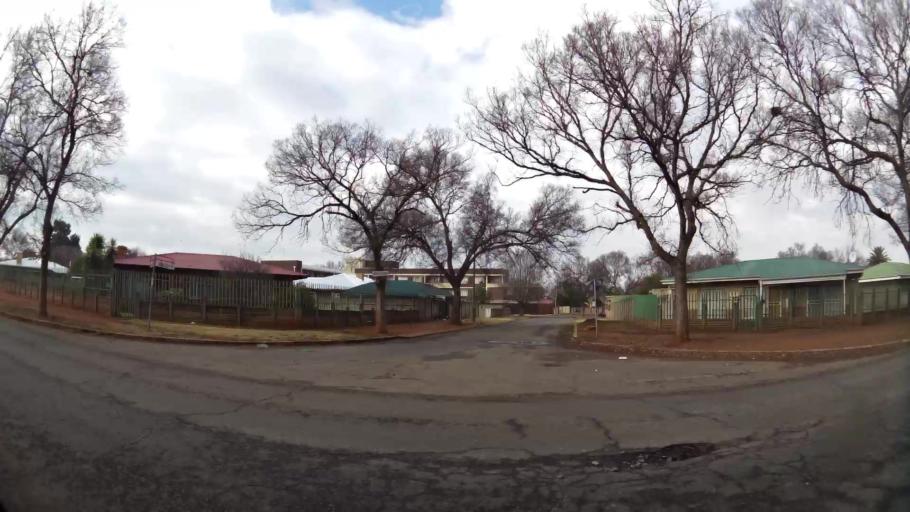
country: ZA
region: Gauteng
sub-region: Sedibeng District Municipality
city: Vanderbijlpark
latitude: -26.7018
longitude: 27.8305
